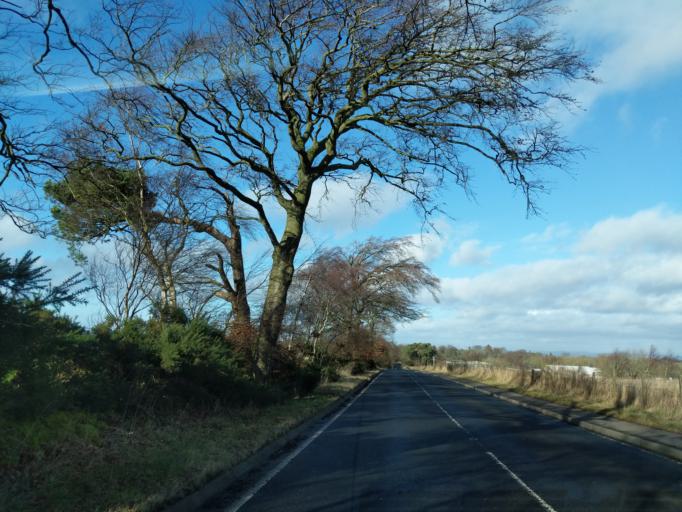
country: GB
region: Scotland
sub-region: West Lothian
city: Kirknewton
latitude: 55.8741
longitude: -3.4094
